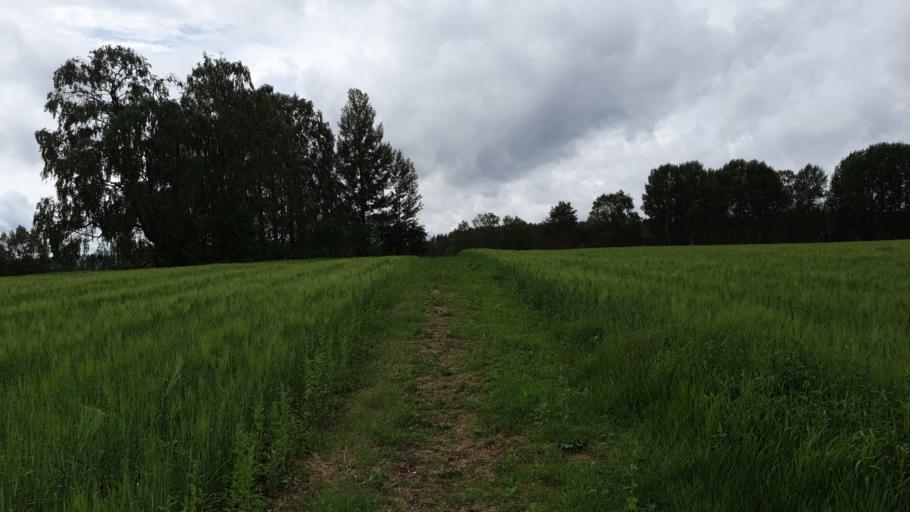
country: FI
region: Kainuu
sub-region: Kehys-Kainuu
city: Kuhmo
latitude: 64.1286
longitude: 29.5694
